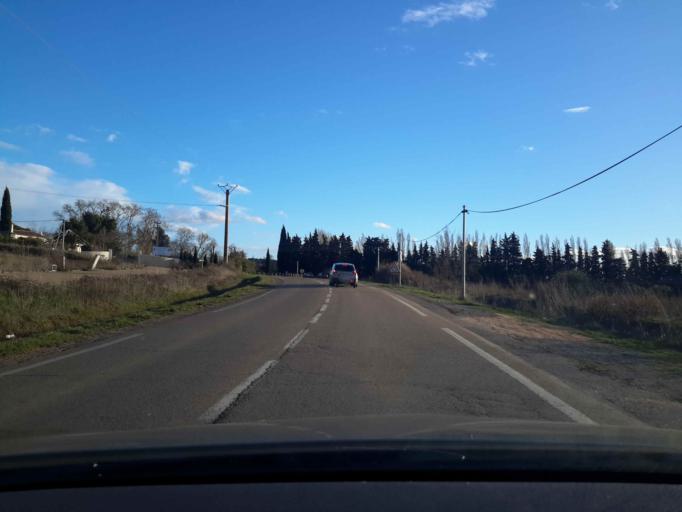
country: FR
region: Languedoc-Roussillon
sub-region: Departement du Gard
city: Generac
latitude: 43.7465
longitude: 4.3415
